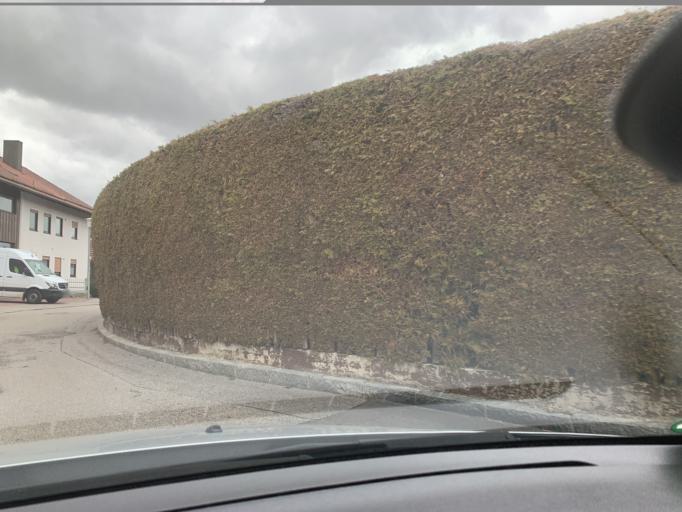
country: DE
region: Bavaria
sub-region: Lower Bavaria
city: Geisenhausen
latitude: 48.4797
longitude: 12.2604
